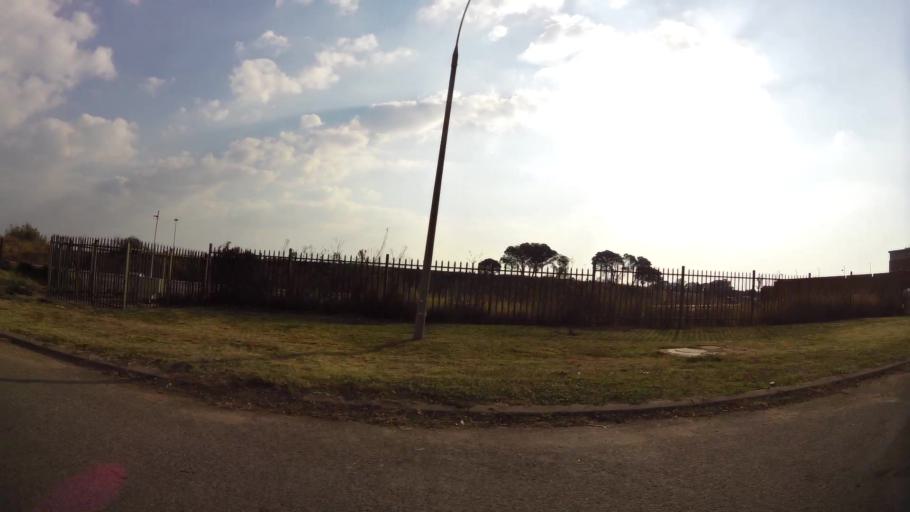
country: ZA
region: Gauteng
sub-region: City of Johannesburg Metropolitan Municipality
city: Modderfontein
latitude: -26.0964
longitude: 28.1947
